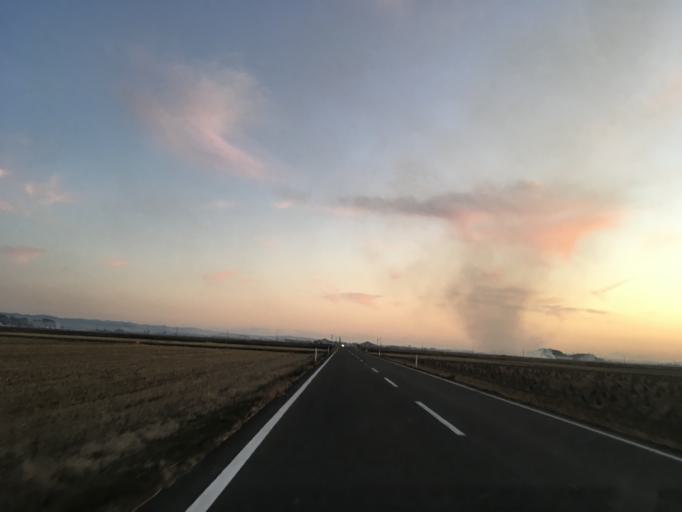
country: JP
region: Iwate
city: Ichinoseki
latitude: 38.7510
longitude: 141.2367
